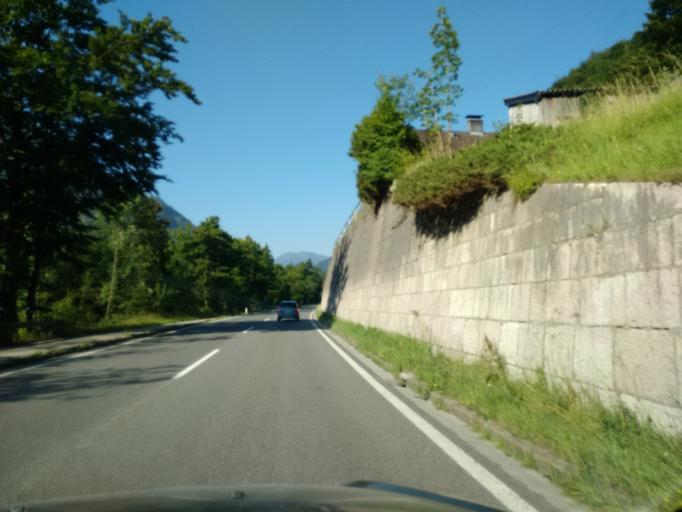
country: AT
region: Upper Austria
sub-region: Politischer Bezirk Gmunden
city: Bad Ischl
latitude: 47.7527
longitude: 13.6958
